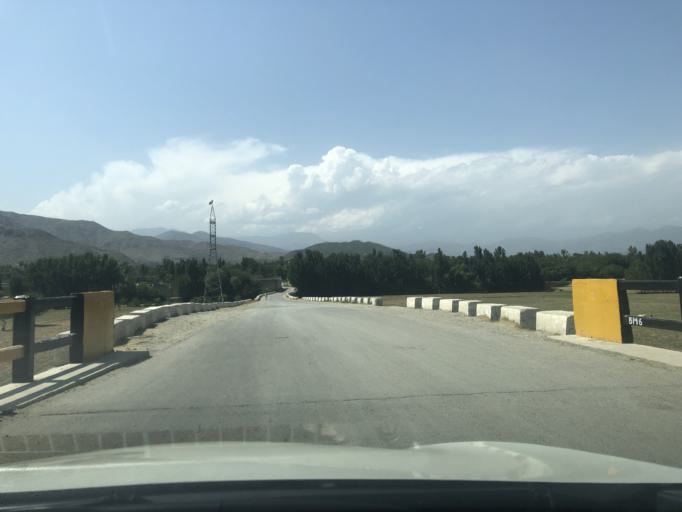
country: PK
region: Khyber Pakhtunkhwa
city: Timurgara
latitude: 34.7937
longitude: 71.6624
